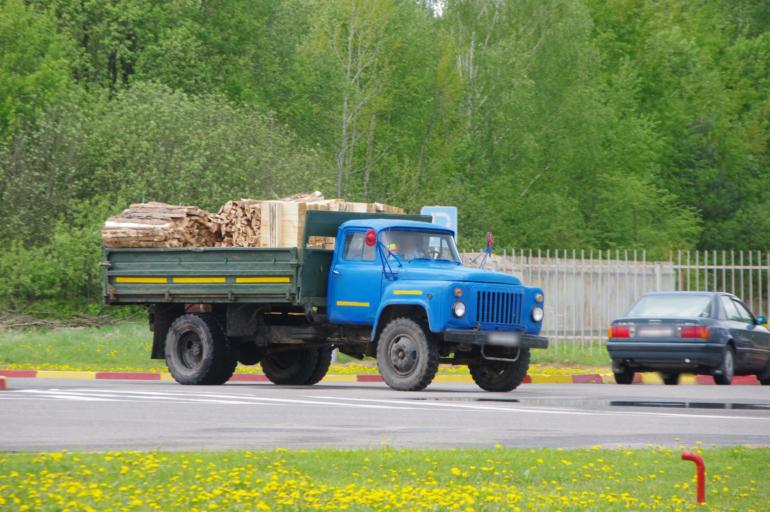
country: BY
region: Minsk
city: Narach
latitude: 54.9119
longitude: 26.7001
